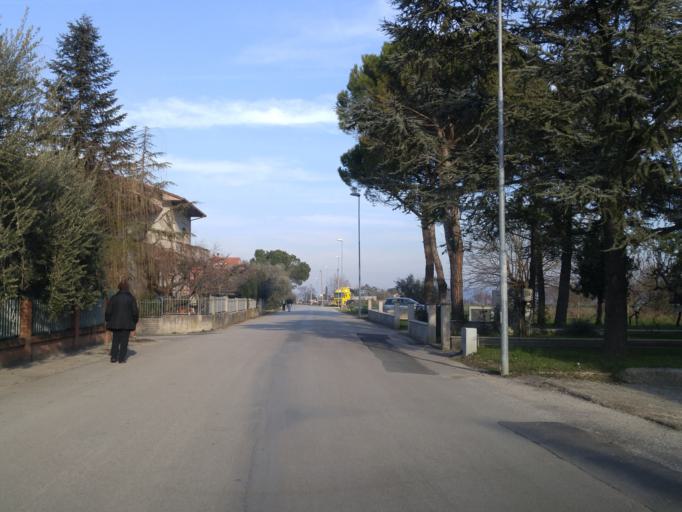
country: IT
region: The Marches
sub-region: Provincia di Pesaro e Urbino
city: Villanova
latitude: 43.7418
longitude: 12.9348
